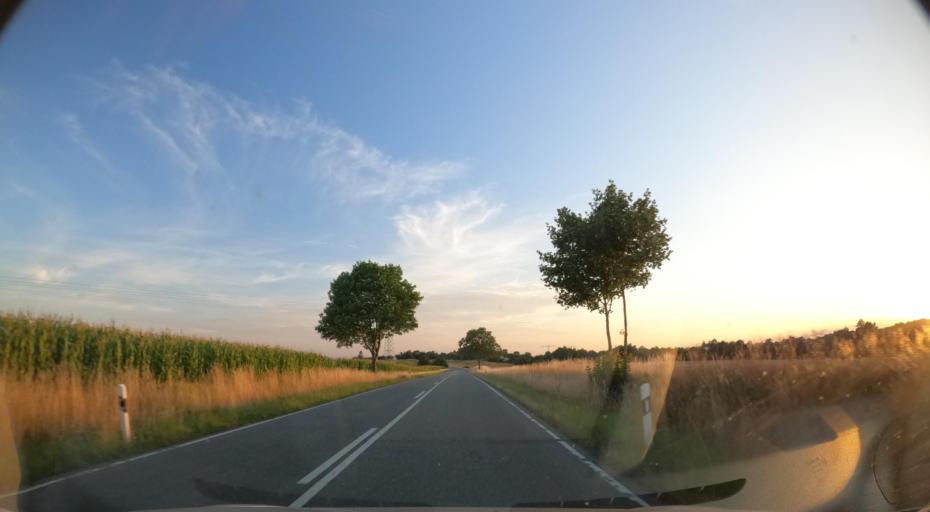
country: DE
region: Mecklenburg-Vorpommern
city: Strasburg
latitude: 53.4859
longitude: 13.6774
